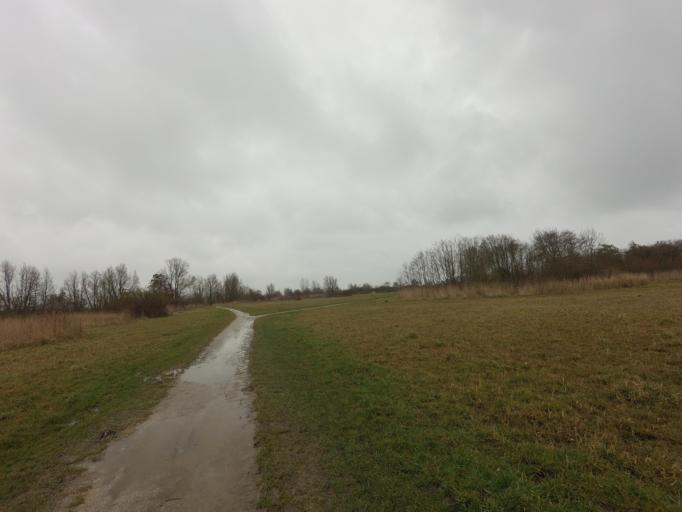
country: NL
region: Friesland
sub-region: Sudwest Fryslan
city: Makkum
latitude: 53.0512
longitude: 5.3914
